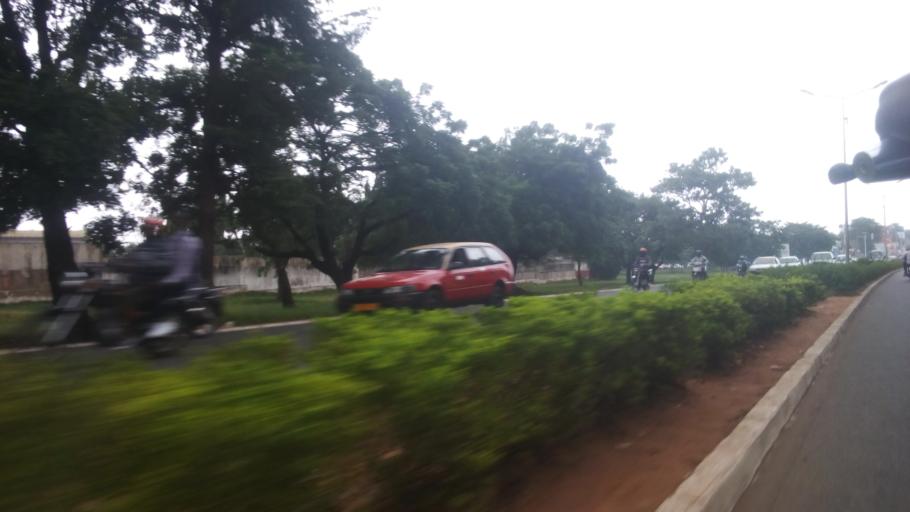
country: TG
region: Maritime
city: Lome
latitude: 6.1696
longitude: 1.2208
